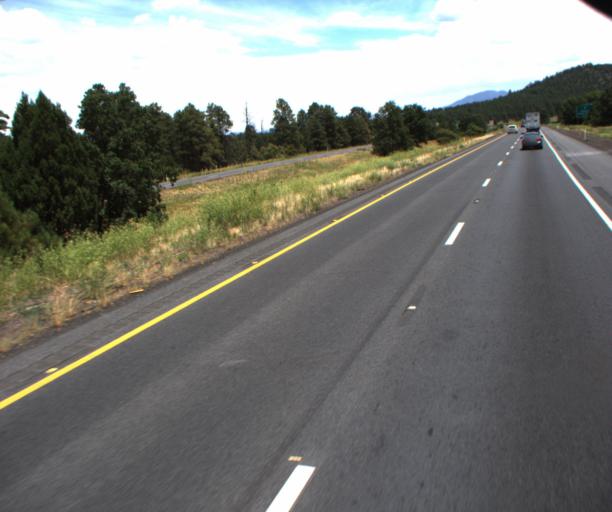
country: US
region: Arizona
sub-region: Coconino County
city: Williams
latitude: 35.2353
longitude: -112.2267
